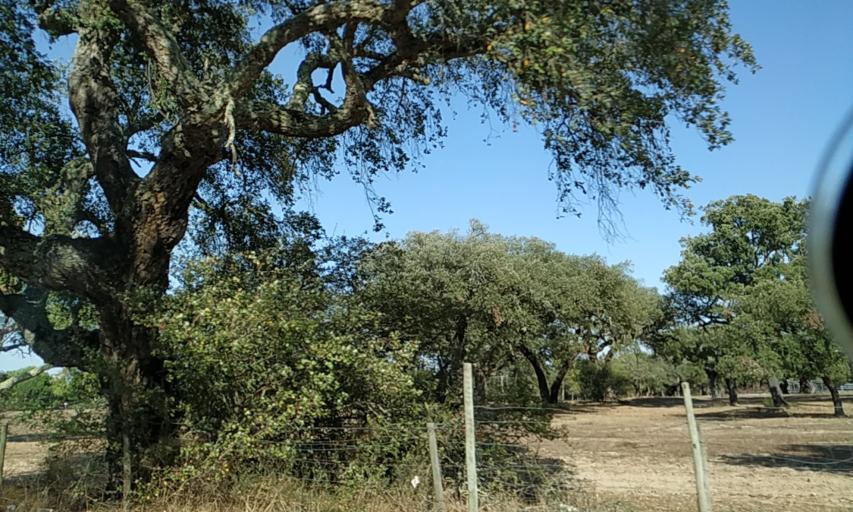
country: PT
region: Santarem
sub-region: Coruche
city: Coruche
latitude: 38.9239
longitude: -8.5231
